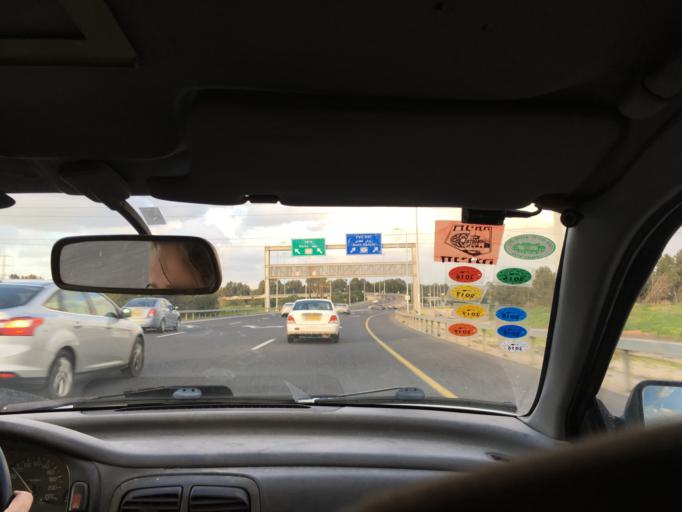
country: IL
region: Tel Aviv
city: Ramat HaSharon
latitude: 32.1350
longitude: 34.8109
